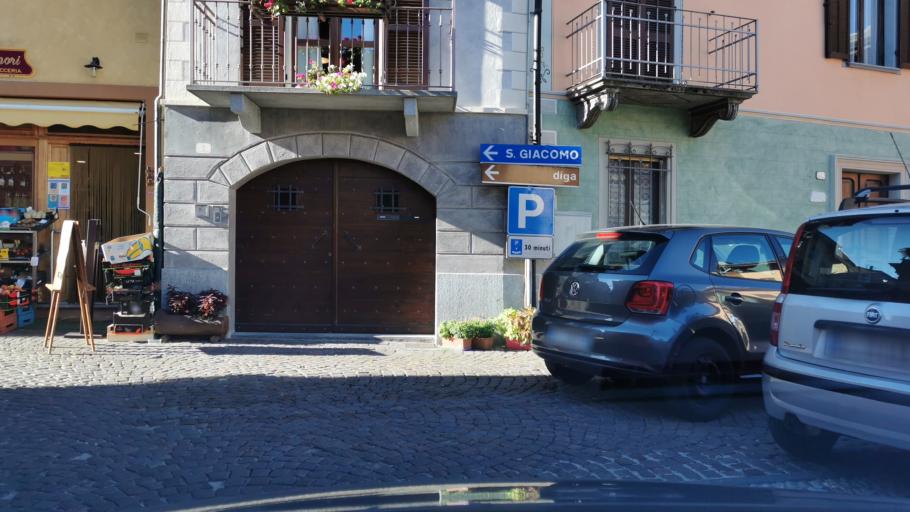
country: IT
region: Piedmont
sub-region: Provincia di Cuneo
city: Entracque
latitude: 44.2383
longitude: 7.3963
